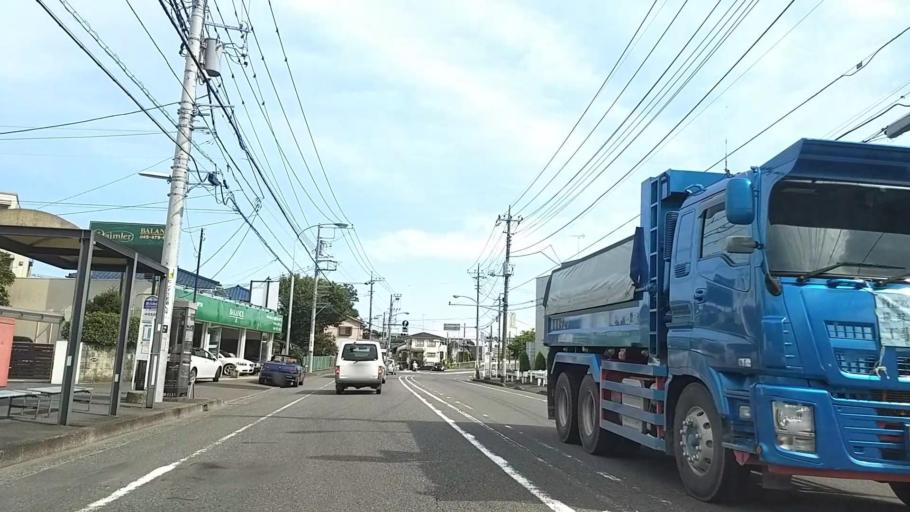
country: JP
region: Kanagawa
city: Yokohama
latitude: 35.5150
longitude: 139.5825
